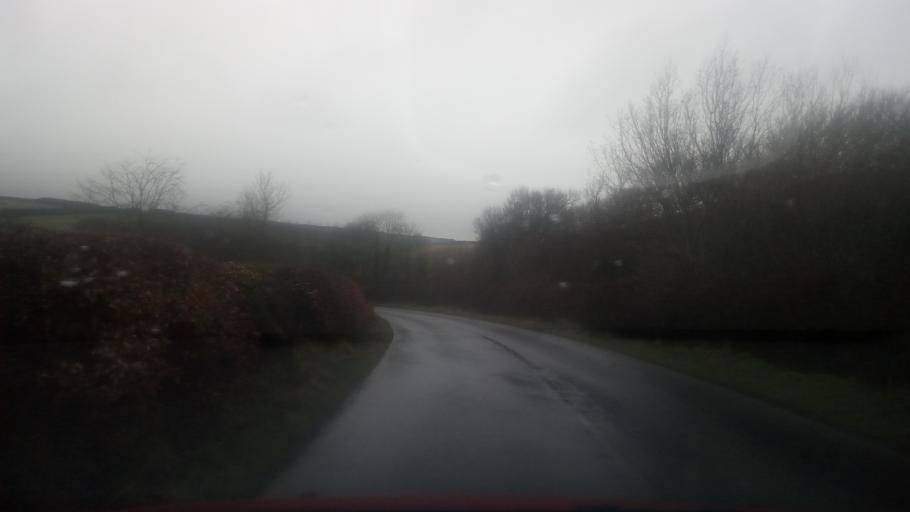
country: GB
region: Scotland
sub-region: The Scottish Borders
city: Earlston
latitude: 55.6140
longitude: -2.6559
